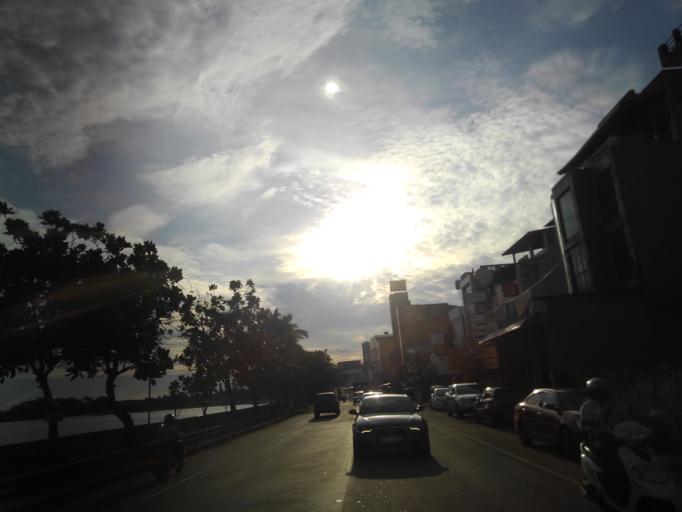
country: LK
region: Southern
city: Galle
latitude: 6.0361
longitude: 80.2218
